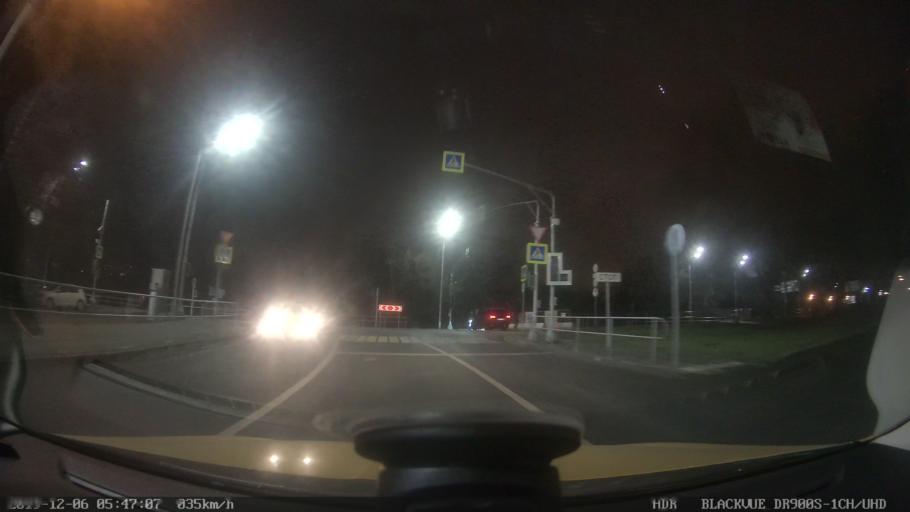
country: RU
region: Moscow
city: Vatutino
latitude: 55.8831
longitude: 37.6617
